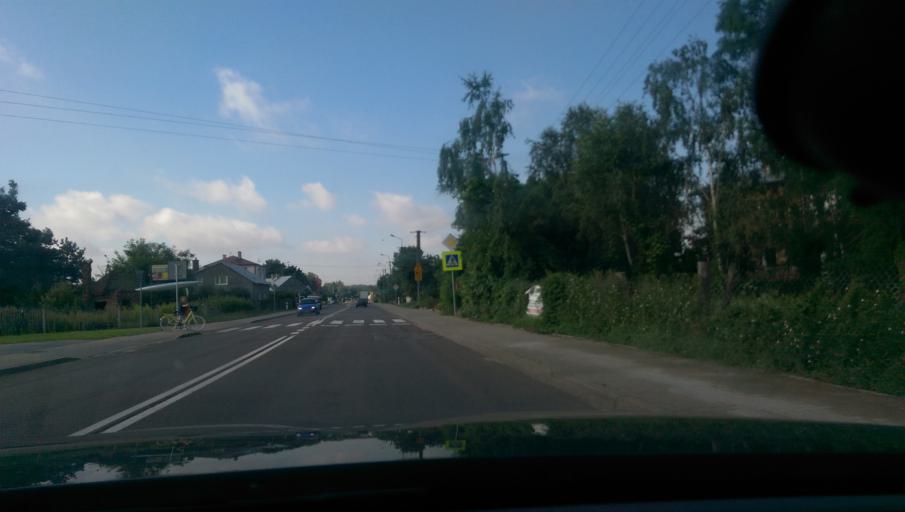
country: PL
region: Masovian Voivodeship
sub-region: Powiat plonski
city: Sochocin
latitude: 52.6892
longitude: 20.4732
